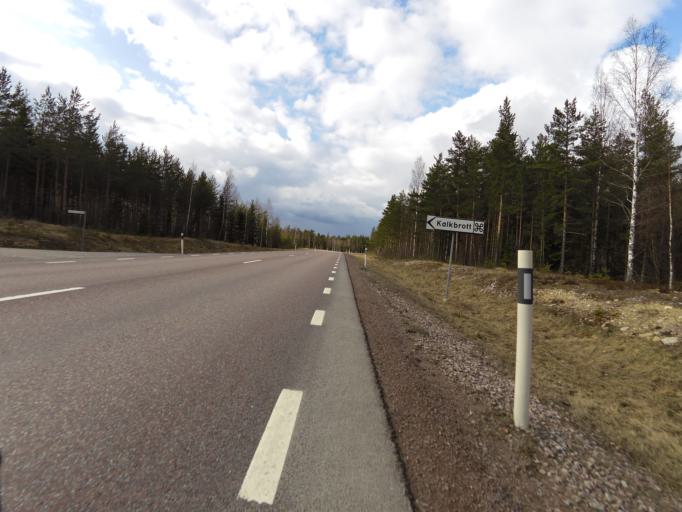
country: SE
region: Gaevleborg
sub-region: Hofors Kommun
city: Hofors
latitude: 60.4931
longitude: 16.4379
